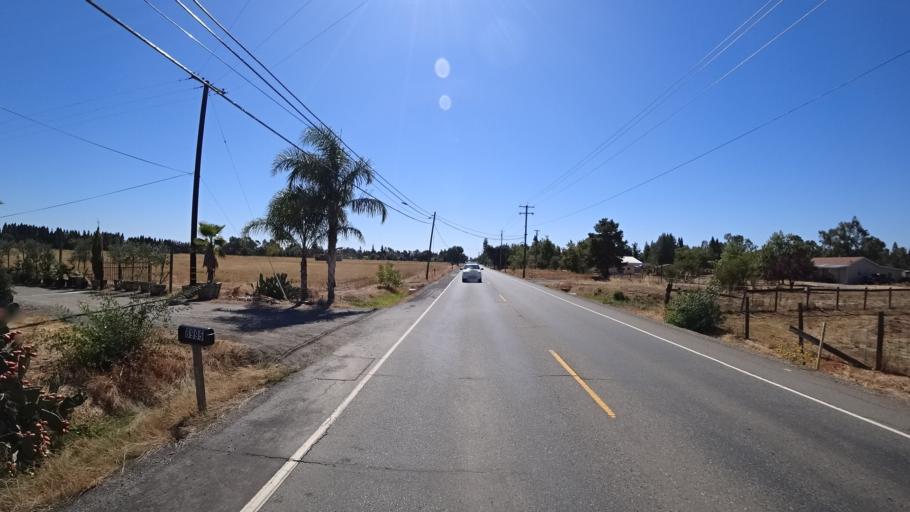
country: US
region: California
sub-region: Sacramento County
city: Vineyard
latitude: 38.4310
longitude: -121.3349
